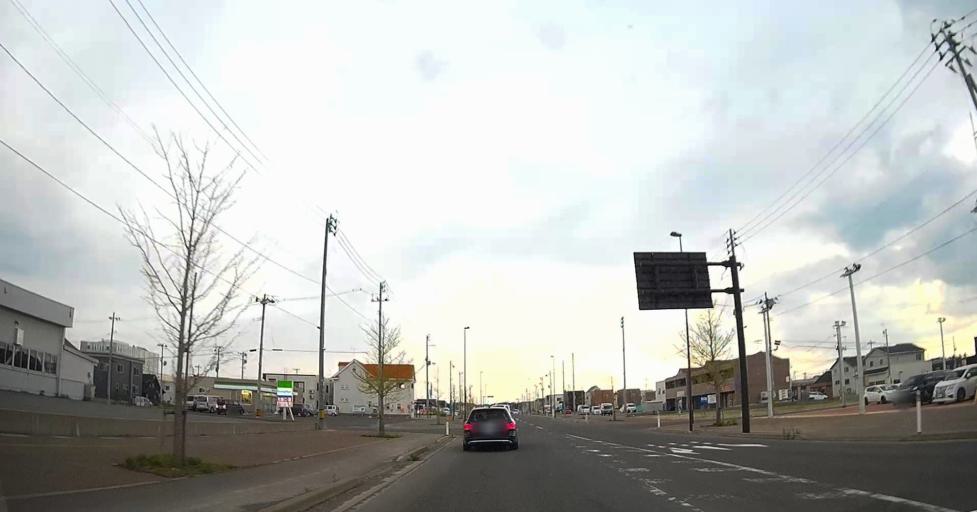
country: JP
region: Aomori
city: Aomori Shi
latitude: 40.8327
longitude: 140.6902
